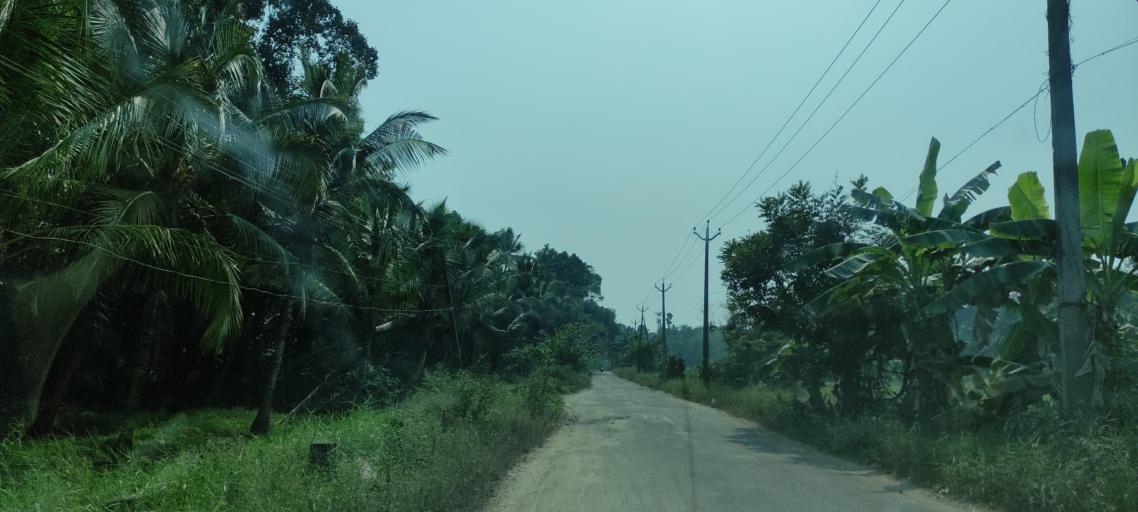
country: IN
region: Kerala
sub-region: Pattanamtitta
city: Tiruvalla
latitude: 9.3477
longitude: 76.5475
